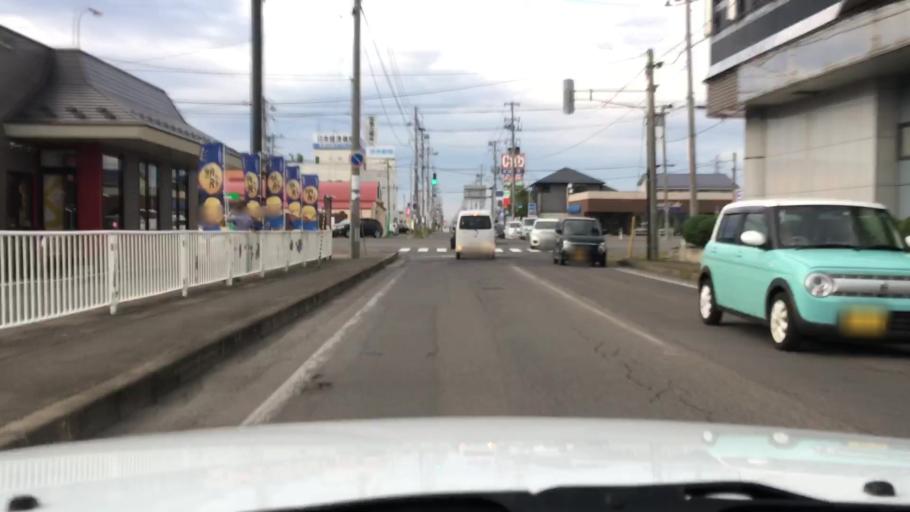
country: JP
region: Aomori
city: Hirosaki
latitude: 40.5964
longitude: 140.5078
